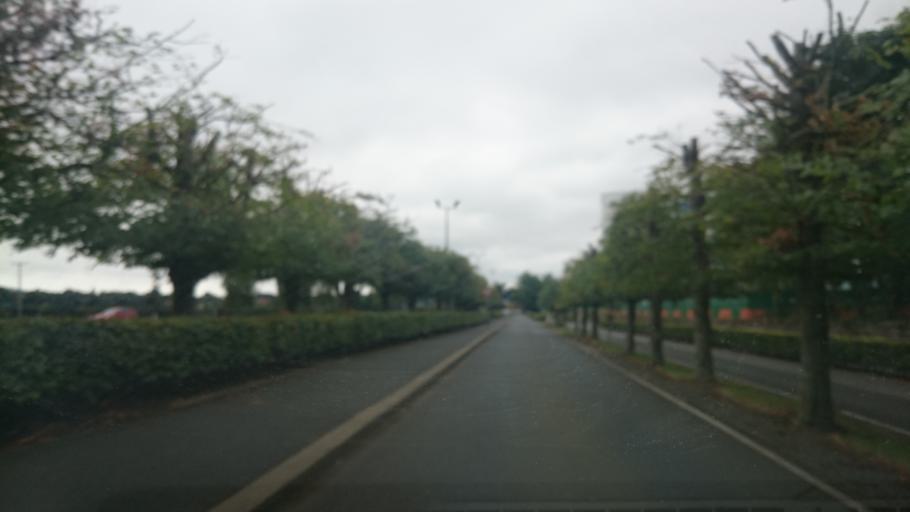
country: IE
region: Leinster
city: Foxrock
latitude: 53.2705
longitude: -6.1966
